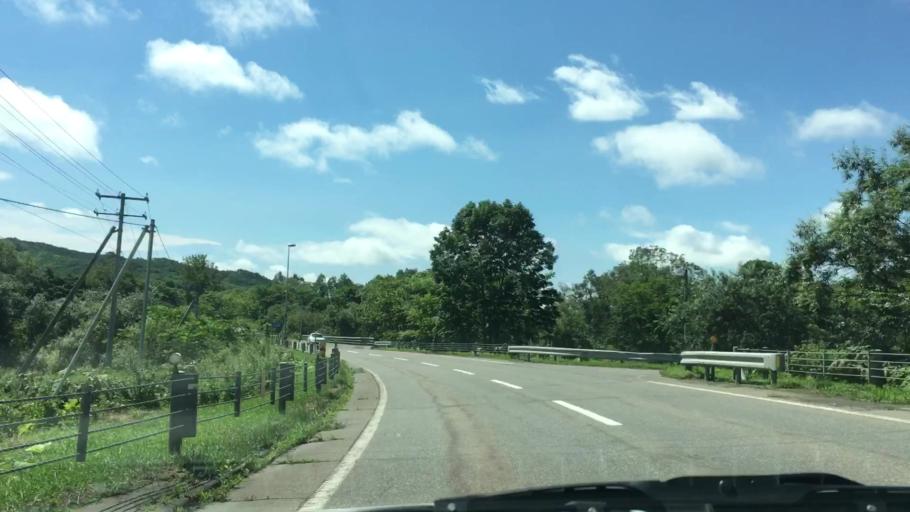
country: JP
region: Hokkaido
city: Kitami
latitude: 43.3366
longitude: 143.7442
